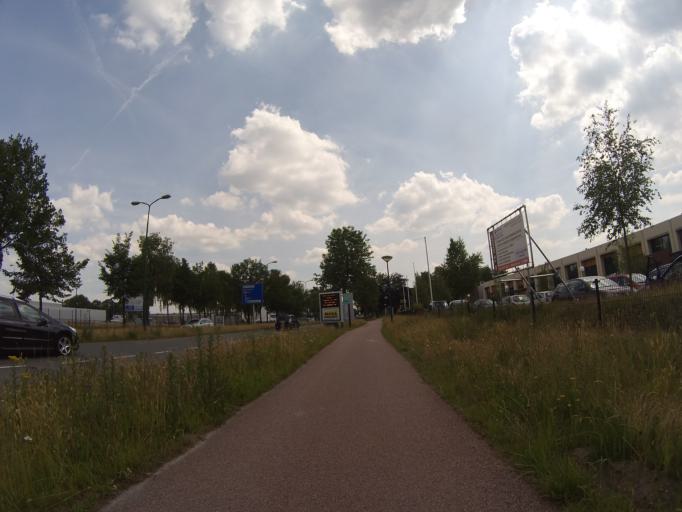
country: NL
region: Utrecht
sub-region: Gemeente Soest
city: Soest
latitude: 52.1812
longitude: 5.2669
